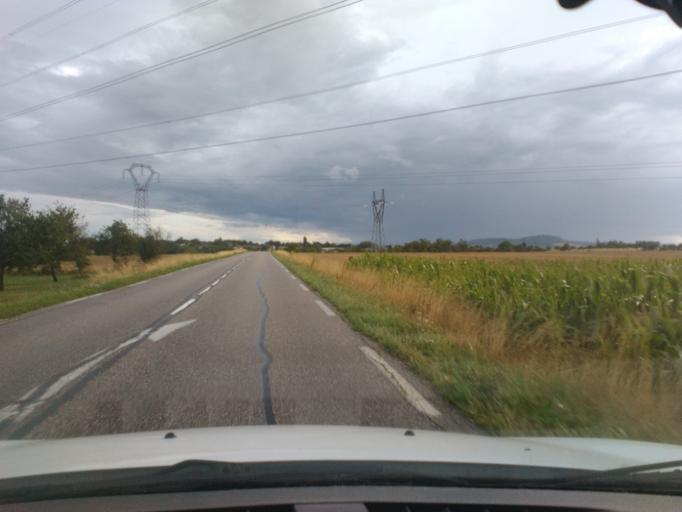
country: FR
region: Lorraine
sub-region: Departement de Meurthe-et-Moselle
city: Vezelise
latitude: 48.4800
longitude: 6.1417
